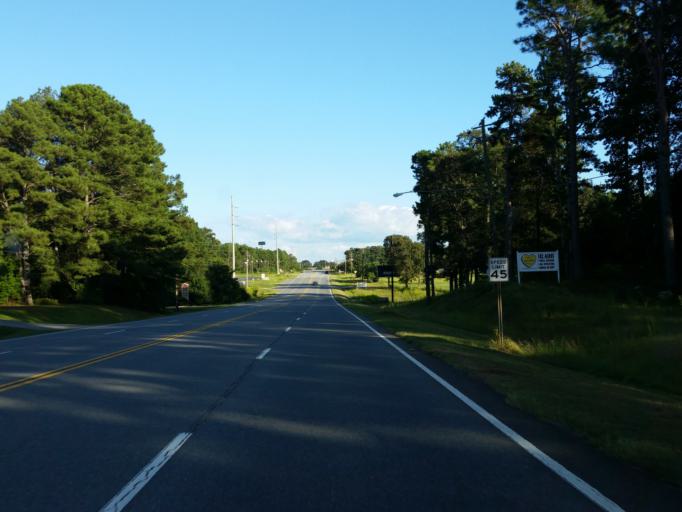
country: US
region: Georgia
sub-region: Houston County
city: Perry
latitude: 32.4781
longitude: -83.7528
